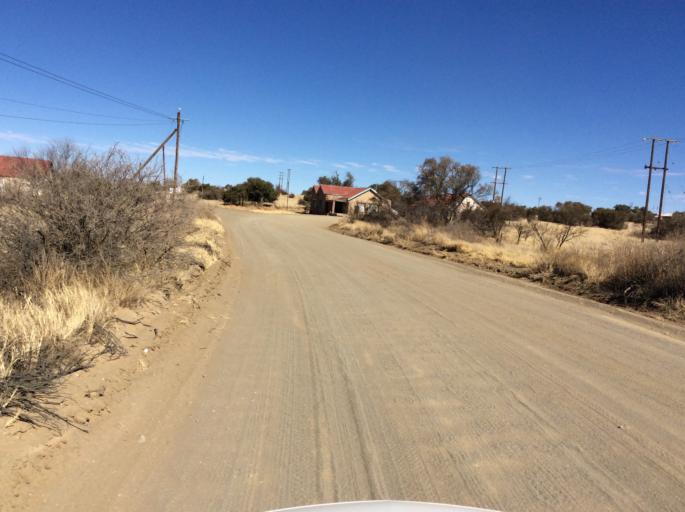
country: ZA
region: Orange Free State
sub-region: Lejweleputswa District Municipality
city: Brandfort
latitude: -28.7183
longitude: 26.0621
